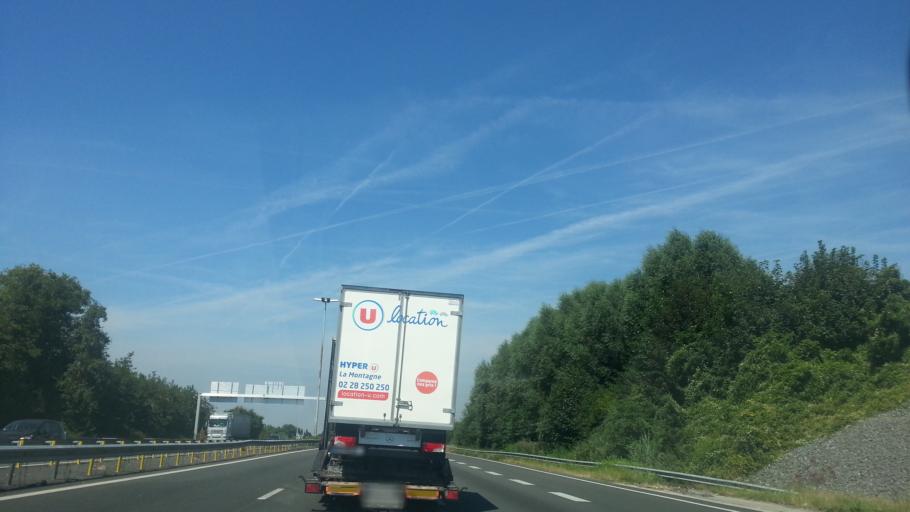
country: FR
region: Ile-de-France
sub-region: Departement du Val-d'Oise
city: Survilliers
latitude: 49.0897
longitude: 2.5508
